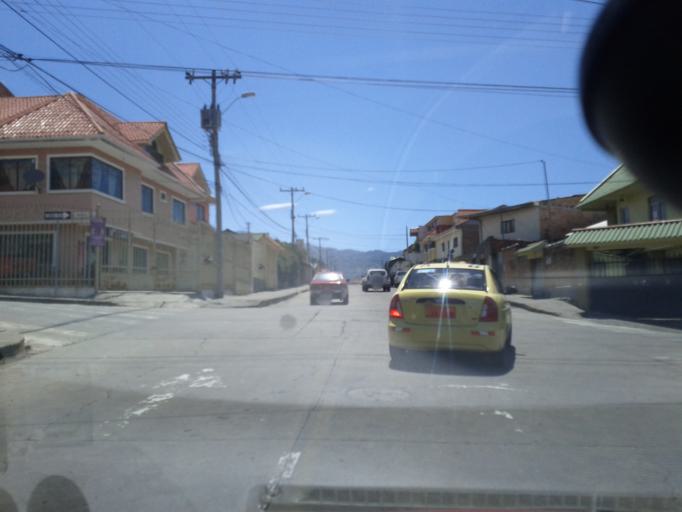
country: EC
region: Azuay
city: Cuenca
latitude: -2.9068
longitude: -79.0175
